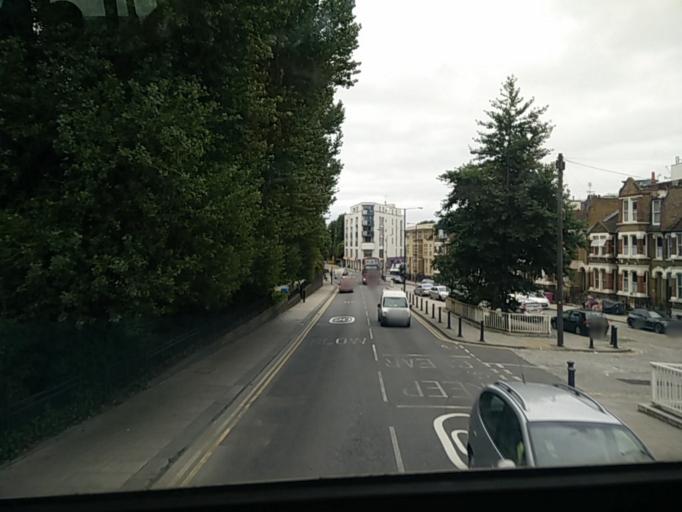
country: GB
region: England
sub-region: Greater London
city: Poplar
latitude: 51.5009
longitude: -0.0088
